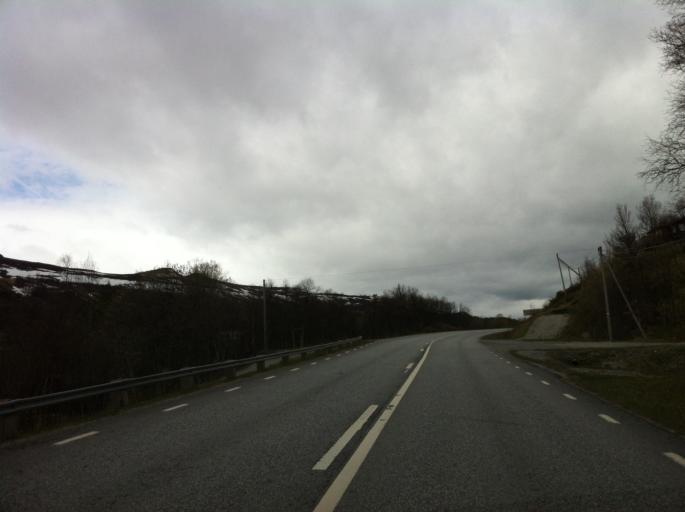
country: NO
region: Sor-Trondelag
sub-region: Tydal
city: Aas
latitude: 62.5602
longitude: 12.2616
